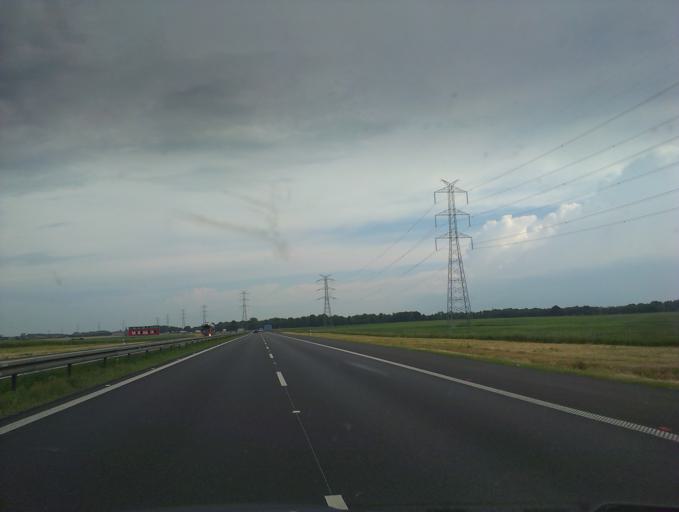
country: PL
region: Opole Voivodeship
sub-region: Powiat brzeski
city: Skarbimierz Osiedle
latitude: 50.7970
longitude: 17.3260
